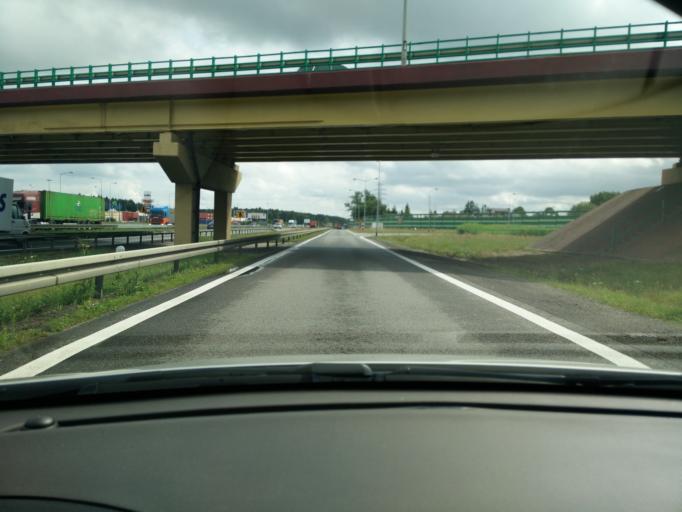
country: PL
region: Pomeranian Voivodeship
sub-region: Gdynia
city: Wielki Kack
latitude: 54.4299
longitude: 18.4875
